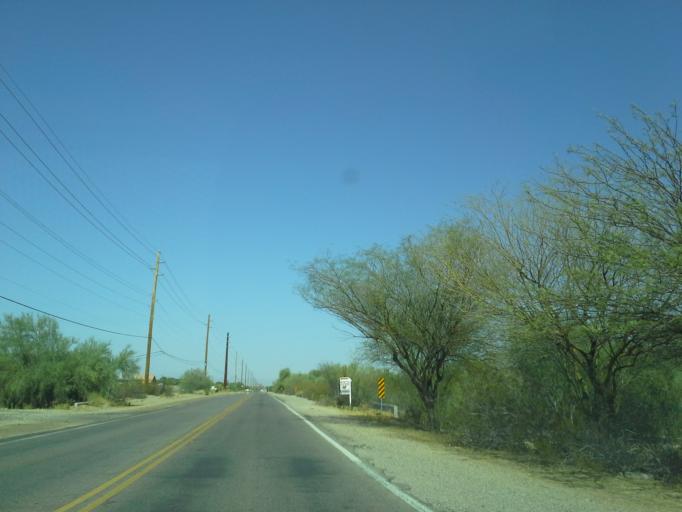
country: US
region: Arizona
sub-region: Maricopa County
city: Queen Creek
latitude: 33.2048
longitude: -111.6659
